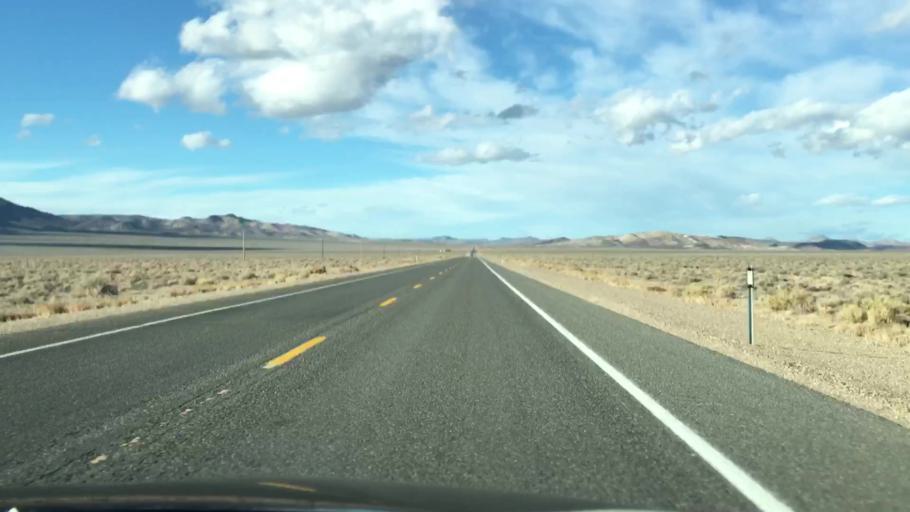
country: US
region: Nevada
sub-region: Esmeralda County
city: Goldfield
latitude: 37.4750
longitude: -117.1774
